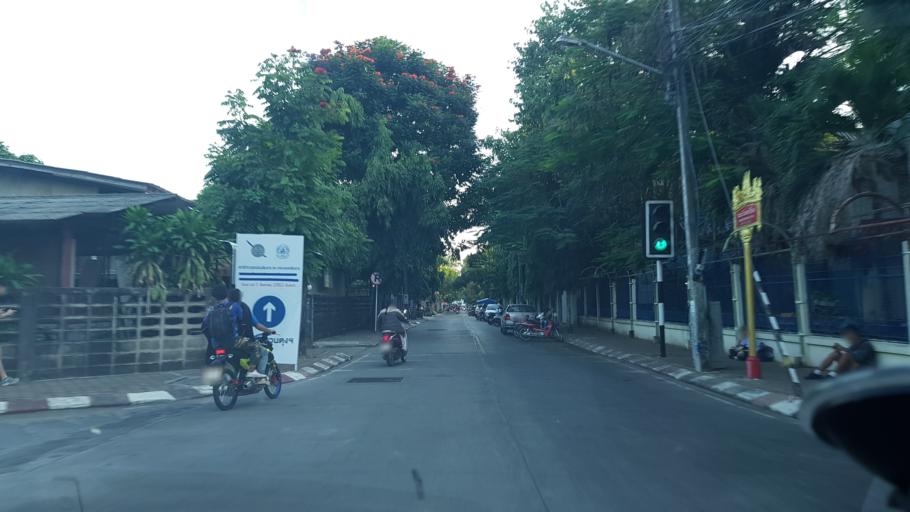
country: TH
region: Chiang Rai
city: Chiang Rai
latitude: 19.9112
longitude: 99.8348
